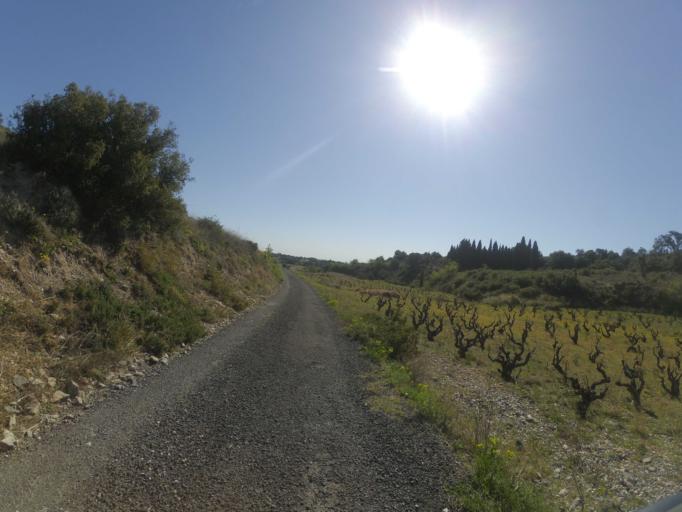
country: FR
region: Languedoc-Roussillon
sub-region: Departement des Pyrenees-Orientales
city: Baixas
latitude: 42.7610
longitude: 2.7676
